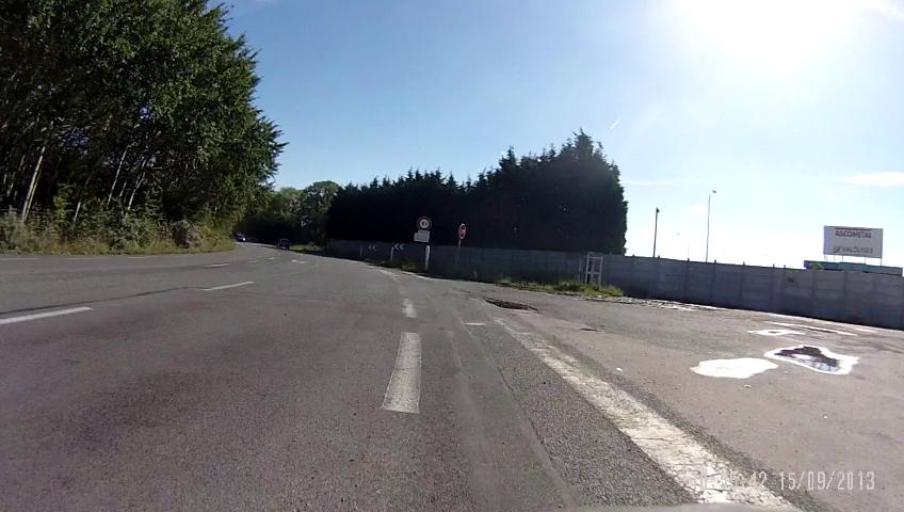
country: FR
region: Nord-Pas-de-Calais
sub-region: Departement du Nord
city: Zuydcoote
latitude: 51.0574
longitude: 2.4721
